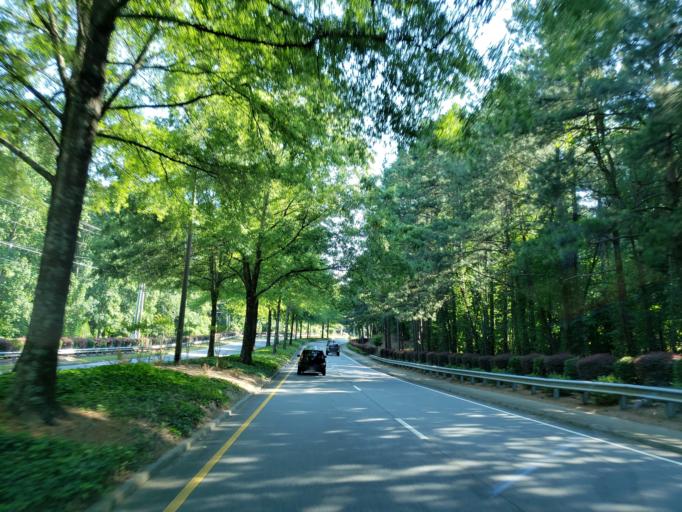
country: US
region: Georgia
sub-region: Cherokee County
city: Woodstock
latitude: 34.1306
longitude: -84.5674
